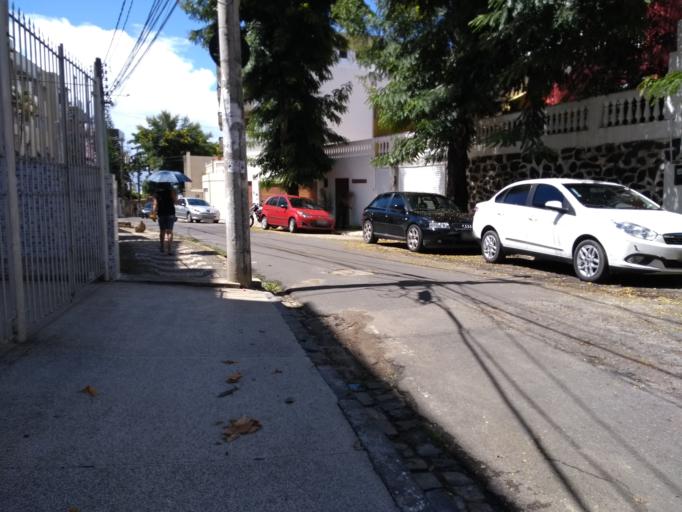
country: BR
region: Bahia
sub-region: Salvador
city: Salvador
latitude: -13.0083
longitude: -38.4891
